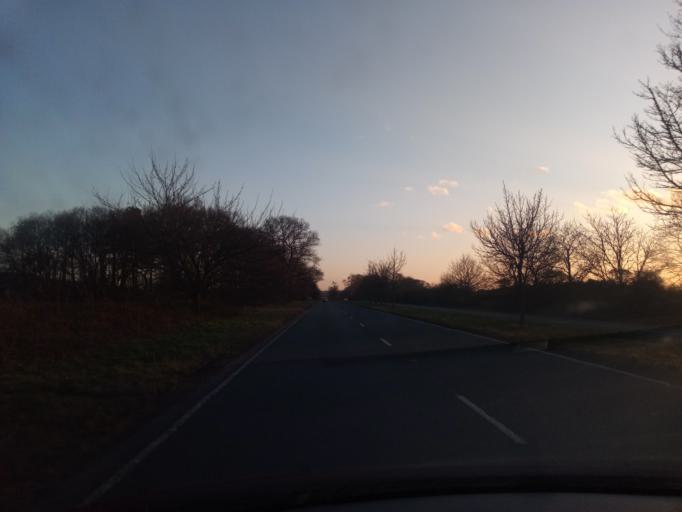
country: GB
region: England
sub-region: Nottinghamshire
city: Farnsfield
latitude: 53.0629
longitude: -1.0703
